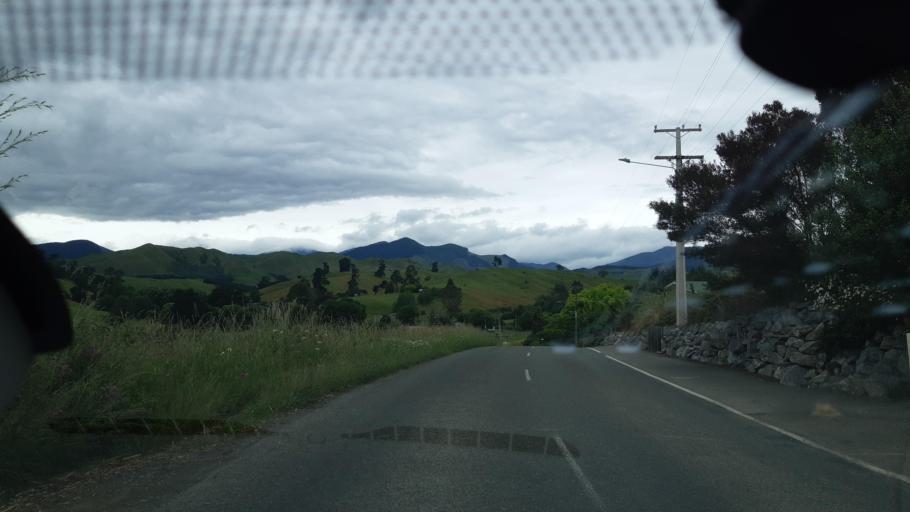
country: NZ
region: Tasman
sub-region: Tasman District
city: Wakefield
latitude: -41.4104
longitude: 173.0485
